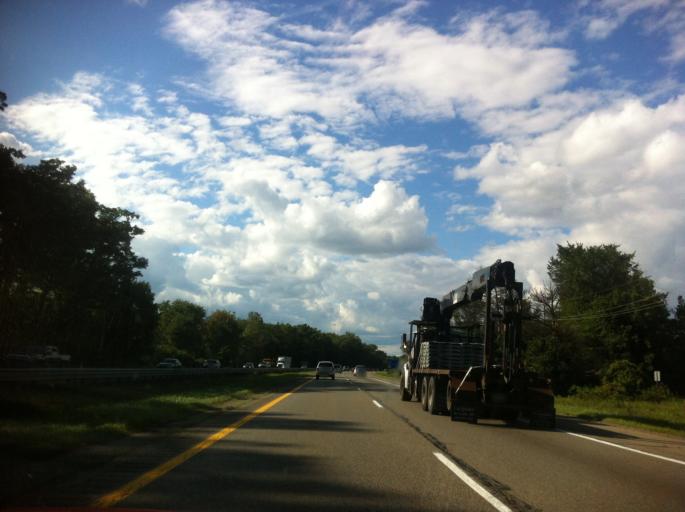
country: US
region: Michigan
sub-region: Livingston County
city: Whitmore Lake
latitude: 42.3857
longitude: -83.7607
